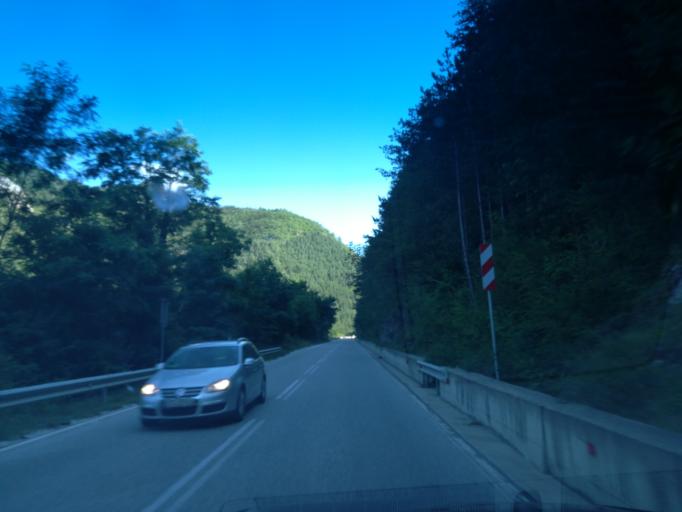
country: BG
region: Smolyan
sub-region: Obshtina Chepelare
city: Chepelare
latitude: 41.8472
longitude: 24.6803
